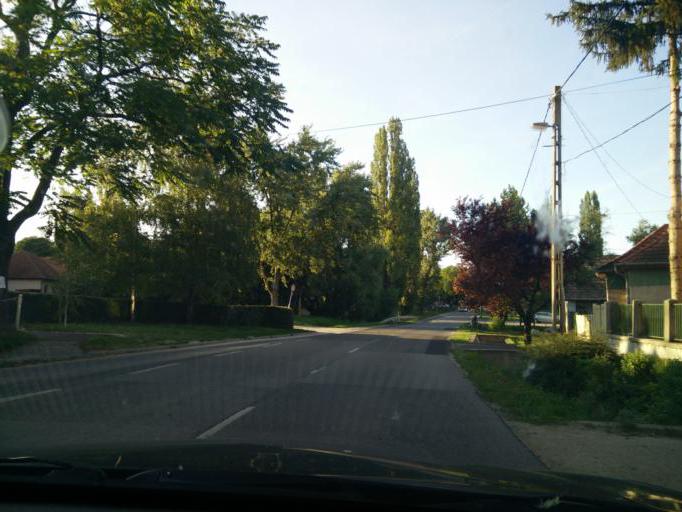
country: HU
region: Pest
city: Zsambek
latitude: 47.5668
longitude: 18.7317
